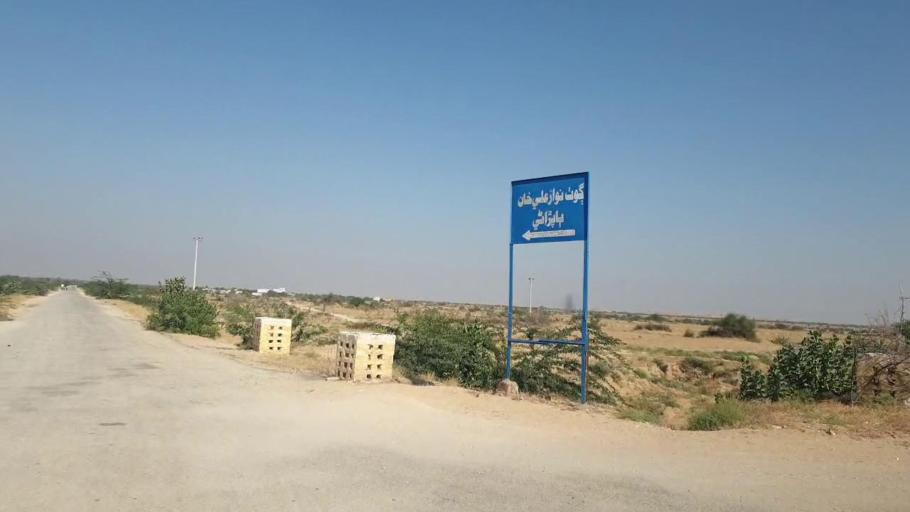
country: PK
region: Sindh
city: Jamshoro
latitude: 25.3702
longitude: 67.8407
